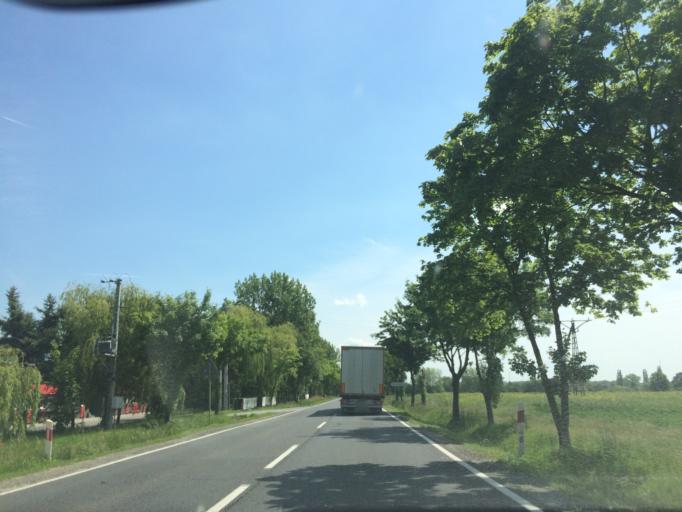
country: PL
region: Lower Silesian Voivodeship
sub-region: Powiat wroclawski
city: Sobotka
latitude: 50.9533
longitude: 16.7667
